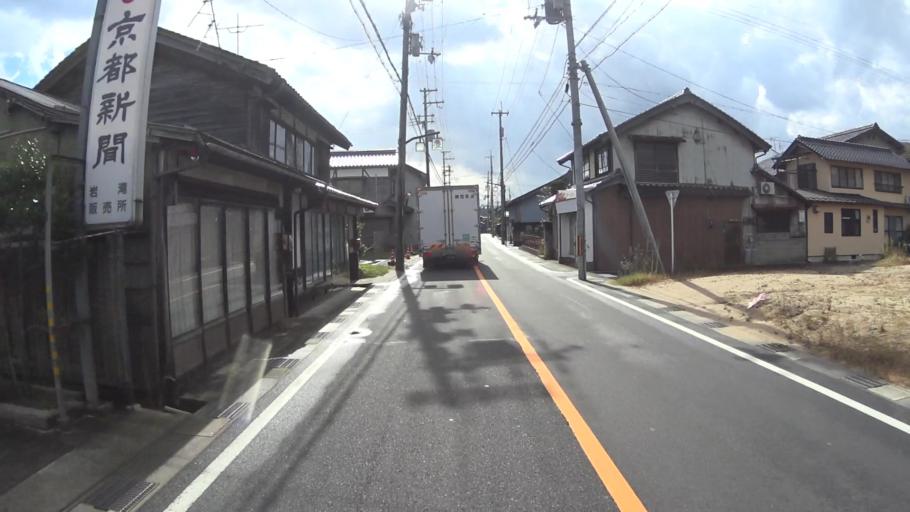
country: JP
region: Kyoto
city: Miyazu
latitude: 35.5675
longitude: 135.1538
